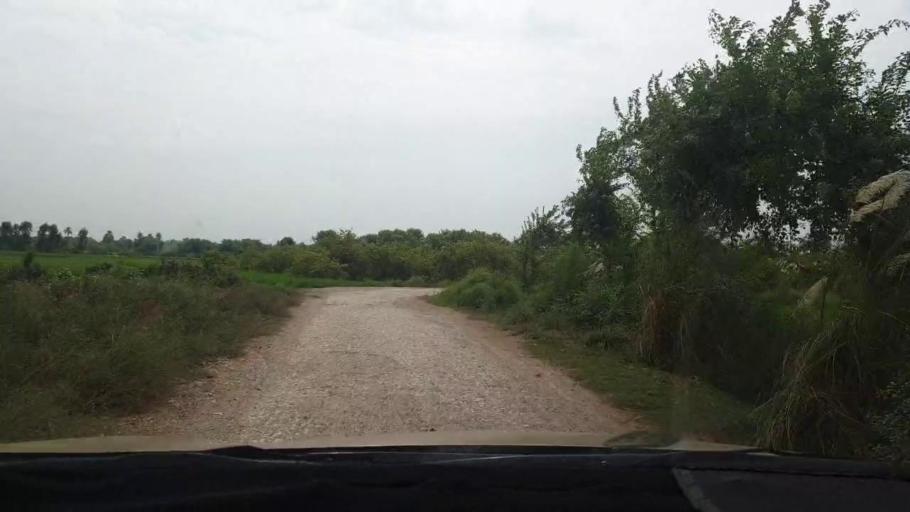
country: PK
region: Sindh
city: Naudero
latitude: 27.6341
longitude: 68.3087
